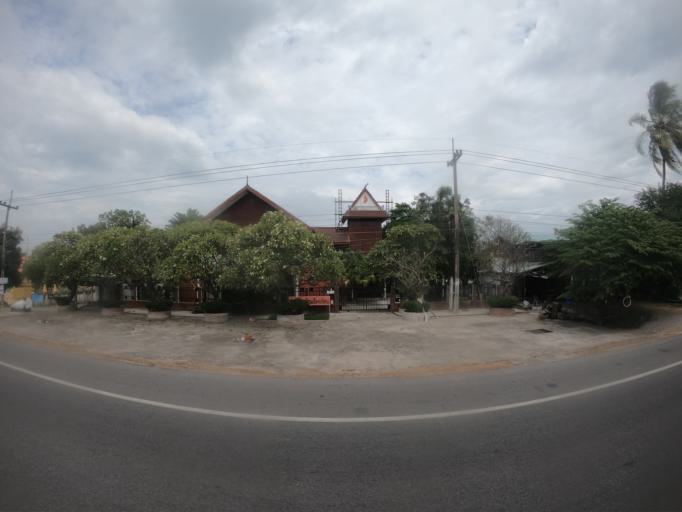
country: TH
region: Maha Sarakham
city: Maha Sarakham
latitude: 16.1544
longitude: 103.3727
